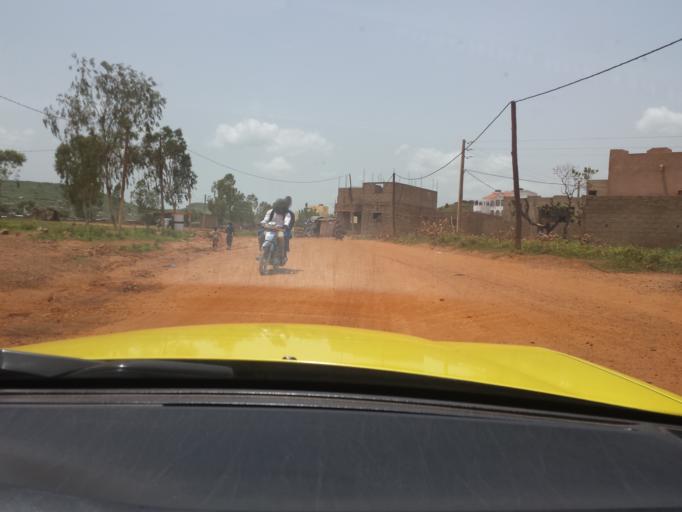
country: ML
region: Bamako
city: Bamako
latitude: 12.6124
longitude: -7.8860
